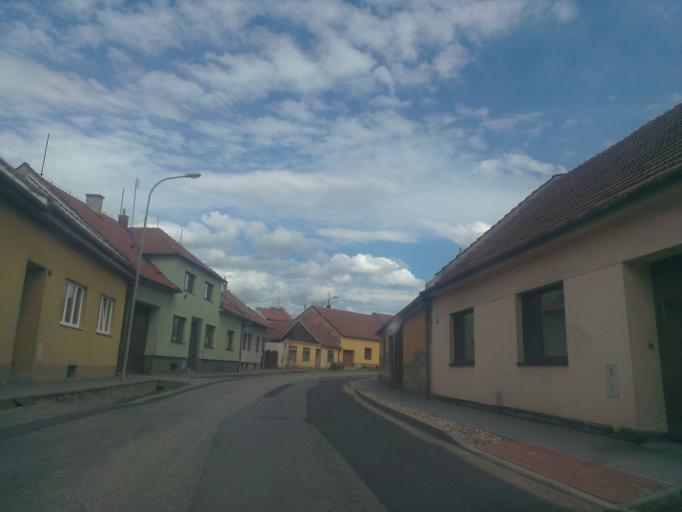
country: CZ
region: South Moravian
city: Orechov
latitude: 49.1112
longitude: 16.5221
